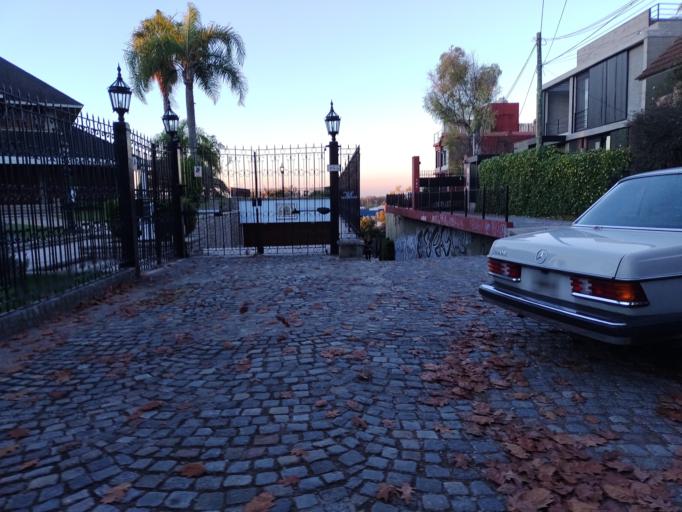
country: AR
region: Buenos Aires
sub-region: Partido de San Isidro
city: San Isidro
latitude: -34.4462
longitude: -58.5387
